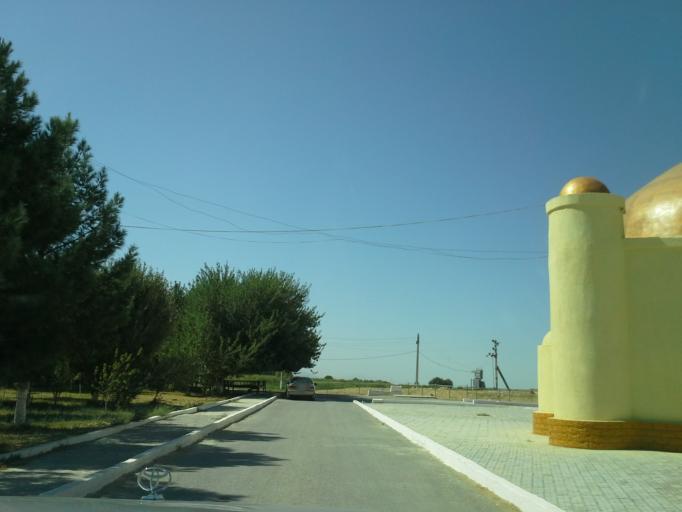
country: TM
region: Ahal
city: Annau
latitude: 37.8948
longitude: 58.5449
